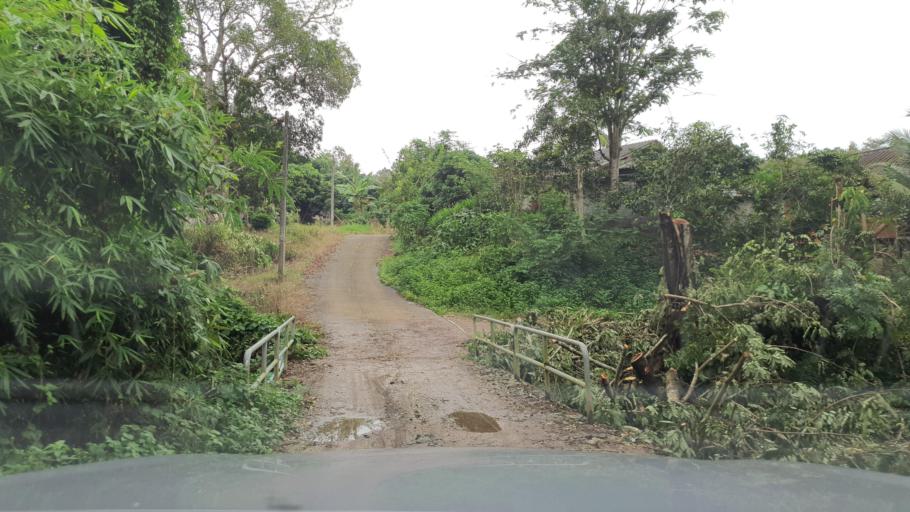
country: TH
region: Chiang Mai
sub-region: Amphoe Chiang Dao
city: Chiang Dao
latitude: 19.3392
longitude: 98.9267
